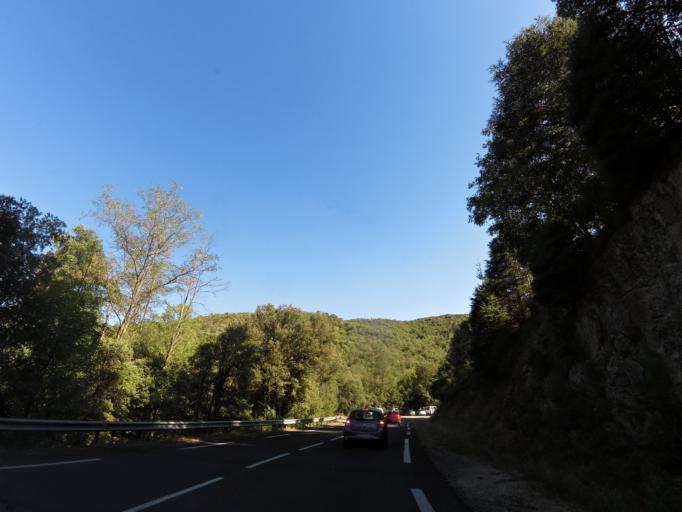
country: FR
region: Languedoc-Roussillon
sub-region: Departement du Gard
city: Valleraugue
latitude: 44.0464
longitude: 3.6863
